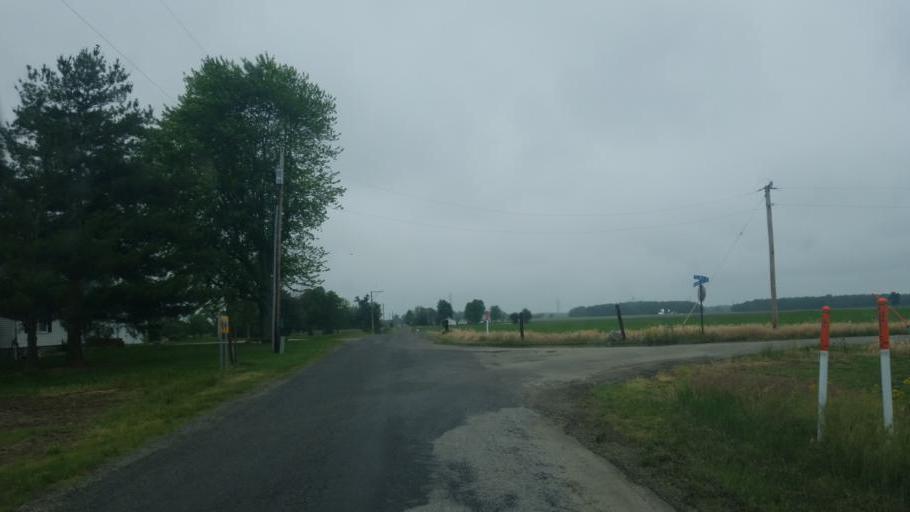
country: US
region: Indiana
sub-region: Marshall County
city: Bremen
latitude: 41.4793
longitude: -86.1421
